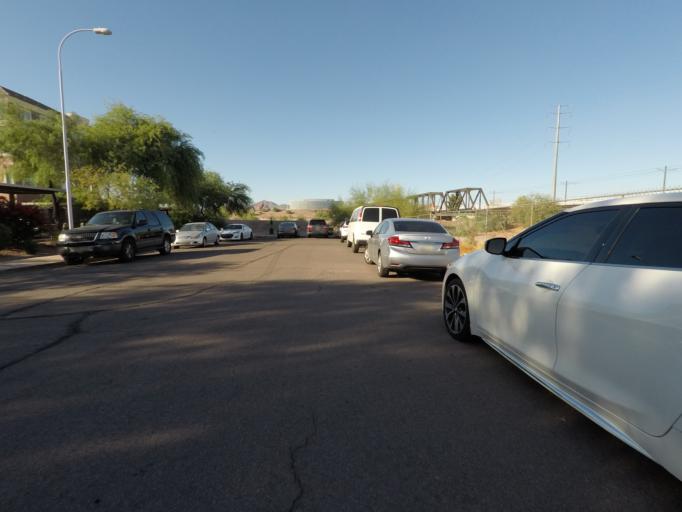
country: US
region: Arizona
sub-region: Maricopa County
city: Tempe Junction
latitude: 33.4305
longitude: -111.9443
